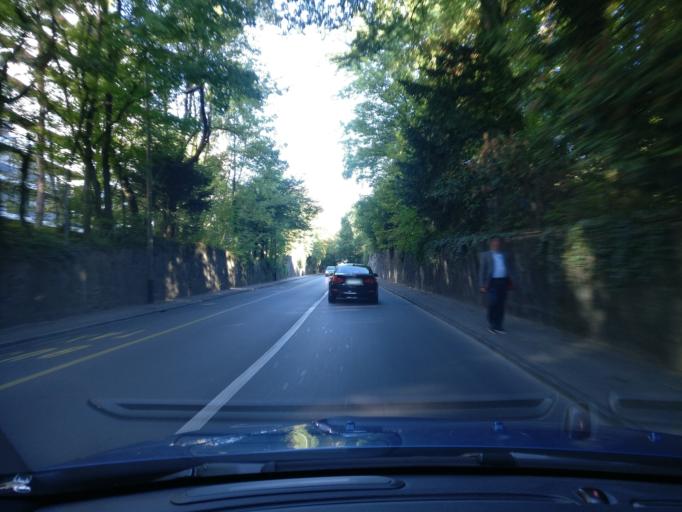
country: CH
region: Geneva
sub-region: Geneva
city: Le Grand-Saconnex
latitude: 46.2264
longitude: 6.1312
